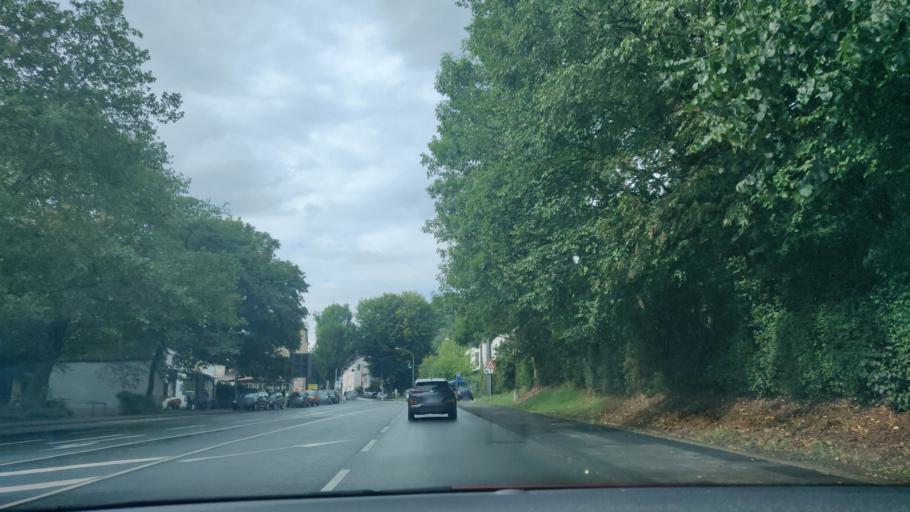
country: DE
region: North Rhine-Westphalia
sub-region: Regierungsbezirk Dusseldorf
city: Wuppertal
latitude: 51.2671
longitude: 7.1294
